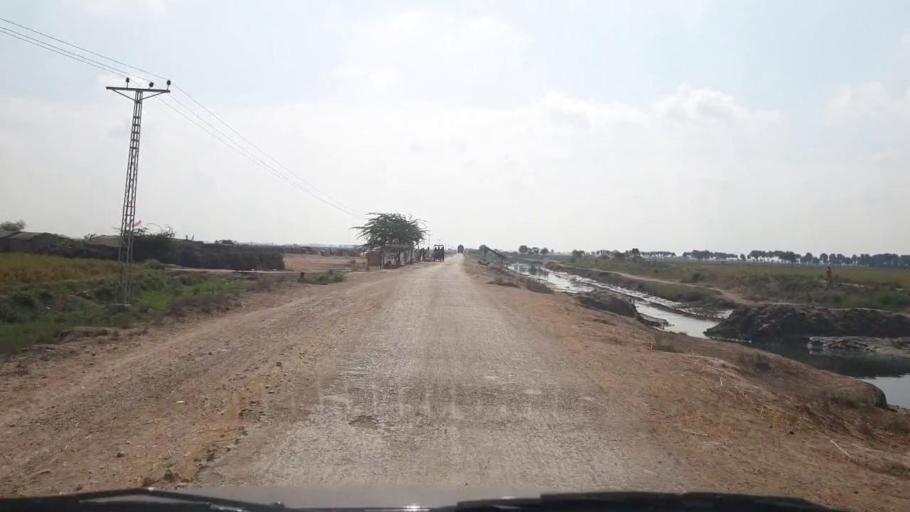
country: PK
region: Sindh
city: Kario
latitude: 24.6292
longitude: 68.5518
